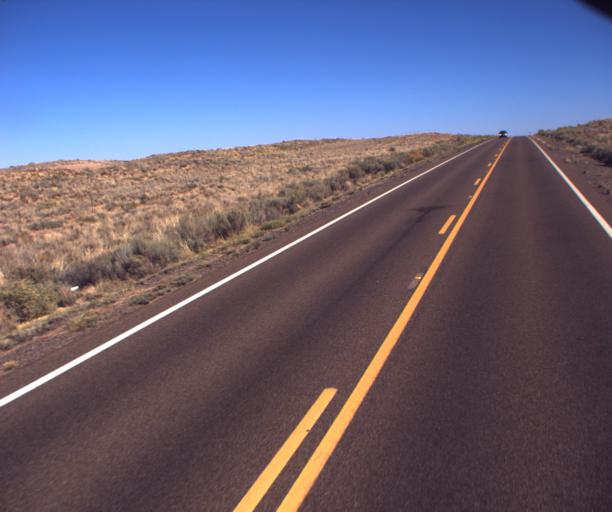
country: US
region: Arizona
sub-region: Navajo County
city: Winslow
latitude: 35.0676
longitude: -110.5757
